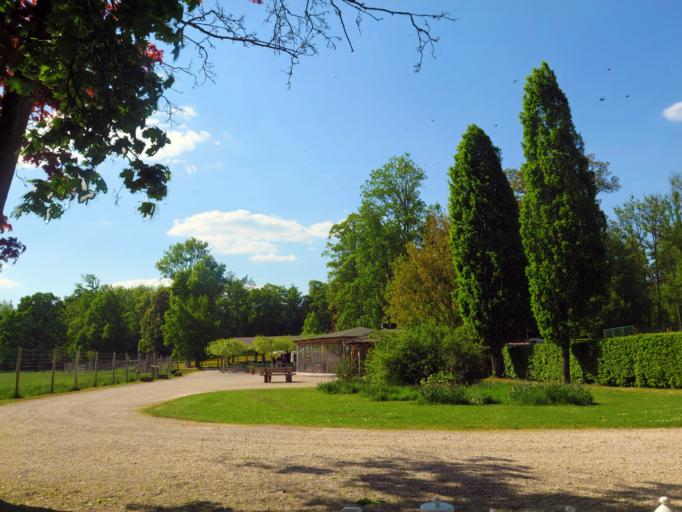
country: DE
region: Bavaria
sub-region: Upper Franconia
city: Weitramsdorf
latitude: 50.2312
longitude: 10.8647
